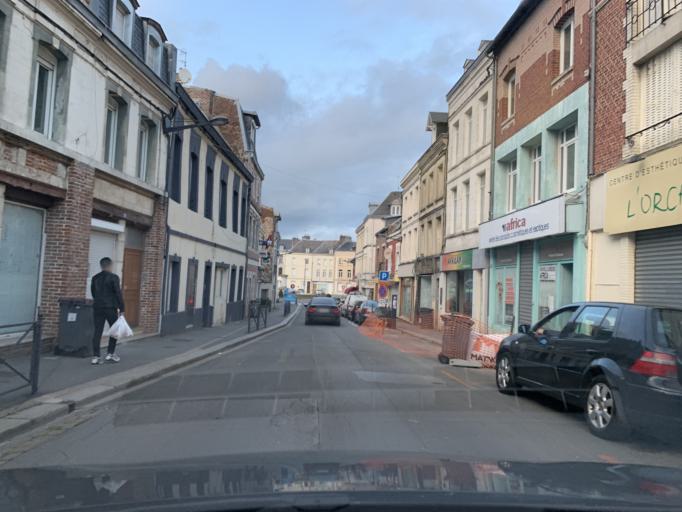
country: FR
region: Picardie
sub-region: Departement de l'Aisne
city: Saint-Quentin
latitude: 49.8503
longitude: 3.2867
